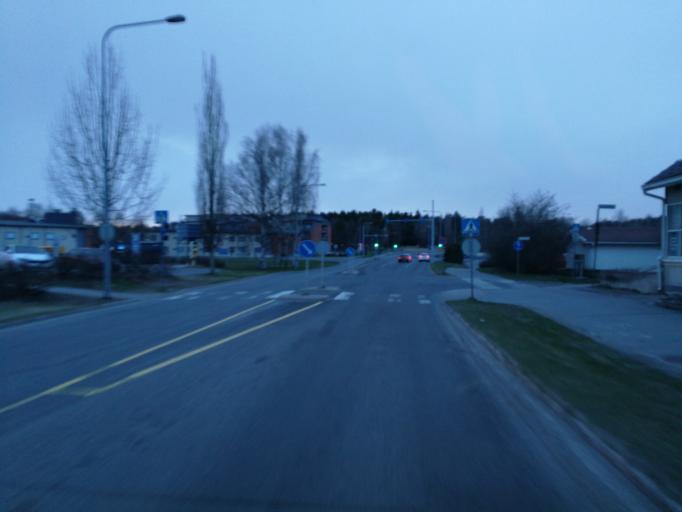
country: FI
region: Varsinais-Suomi
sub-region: Turku
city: Turku
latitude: 60.4731
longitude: 22.2344
